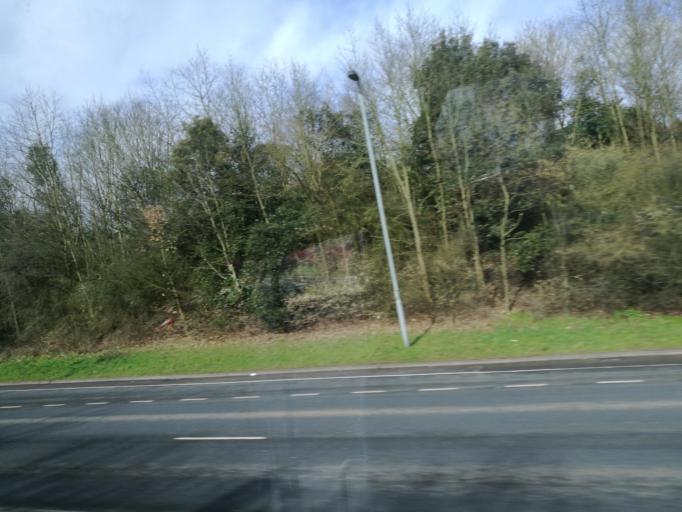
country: GB
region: England
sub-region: Luton
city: Luton
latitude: 51.8635
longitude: -0.4069
